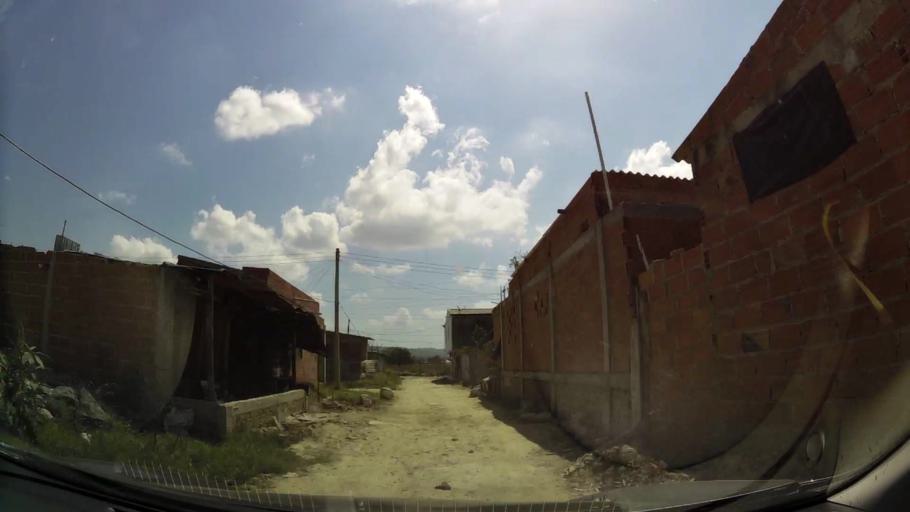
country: CO
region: Bolivar
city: Cartagena
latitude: 10.3555
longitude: -75.4838
